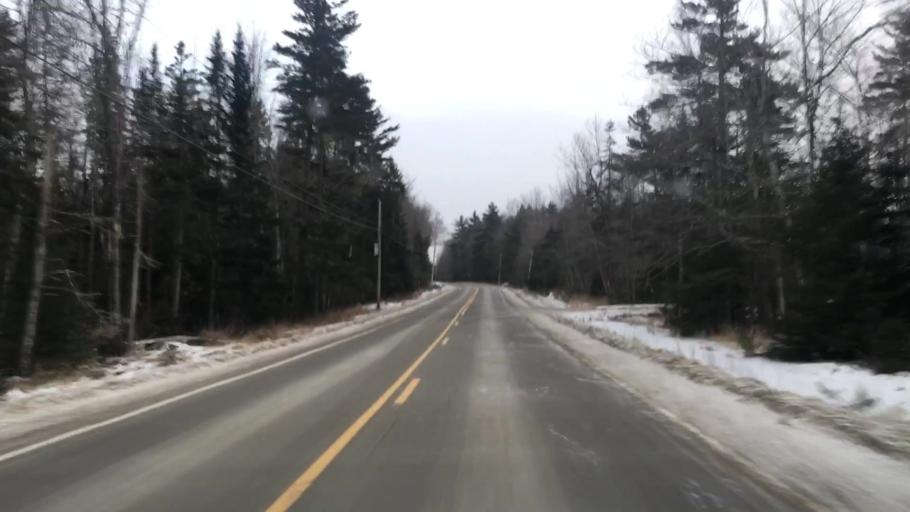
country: US
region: Maine
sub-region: Hancock County
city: Ellsworth
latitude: 44.6196
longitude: -68.3831
